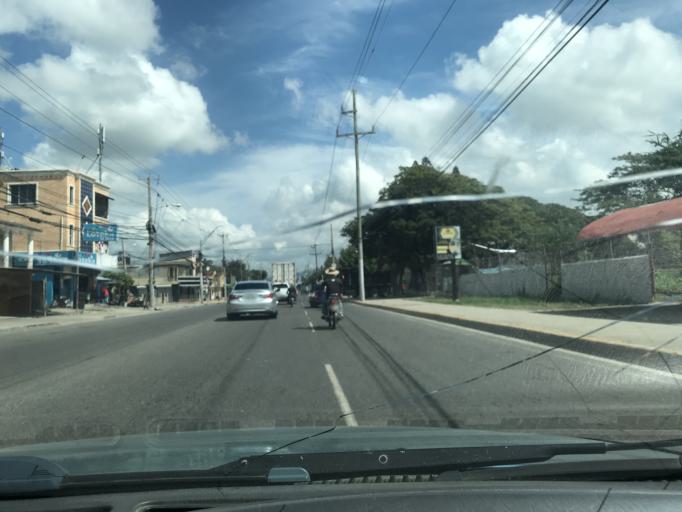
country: DO
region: Santiago
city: Palmar Arriba
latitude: 19.4898
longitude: -70.7349
